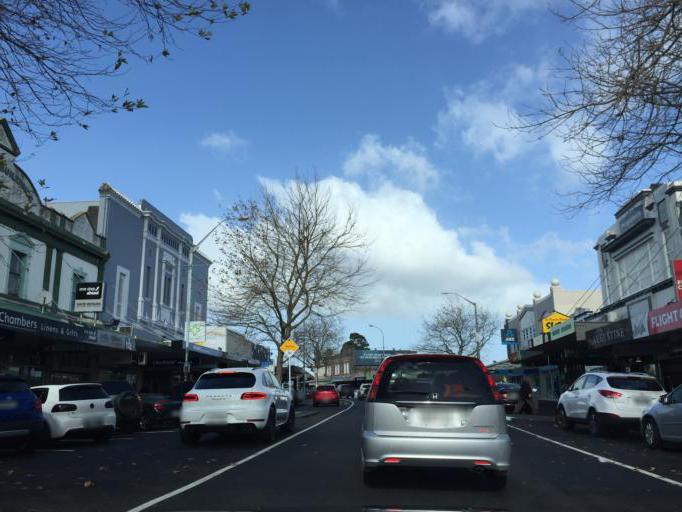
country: NZ
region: Auckland
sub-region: Auckland
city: Auckland
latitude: -36.8478
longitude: 174.7440
